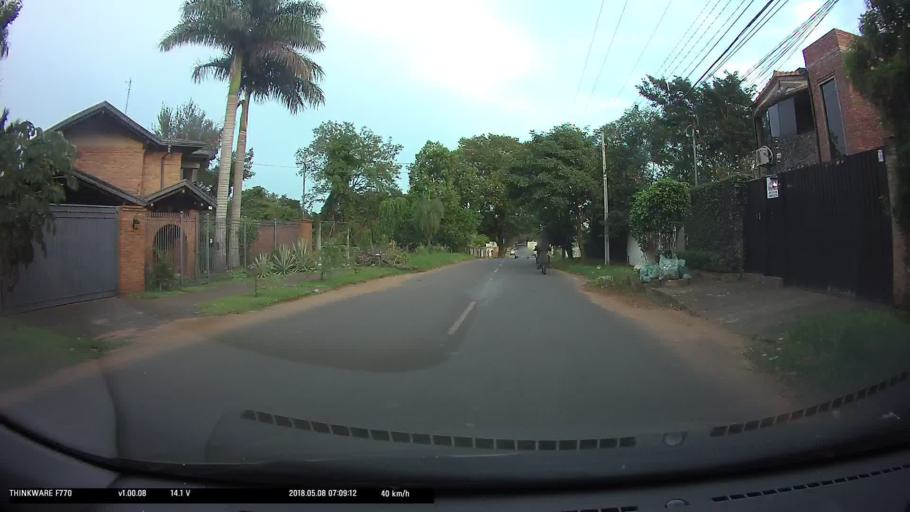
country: PY
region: Central
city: San Lorenzo
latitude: -25.2604
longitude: -57.5042
